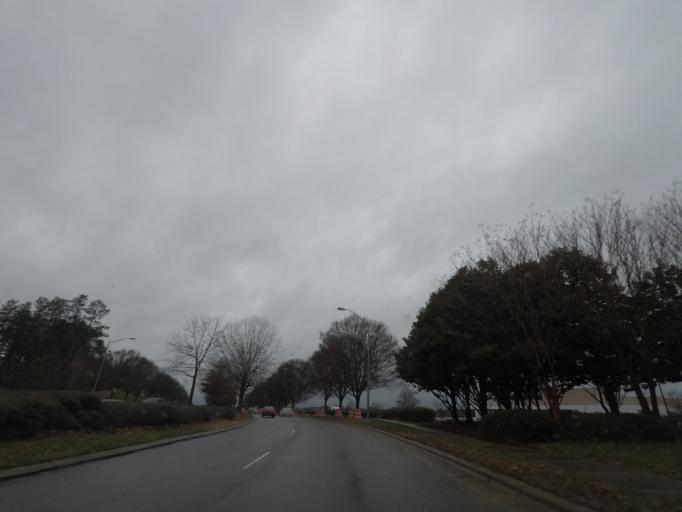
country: US
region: North Carolina
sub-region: Durham County
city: Durham
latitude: 35.9034
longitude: -78.9451
